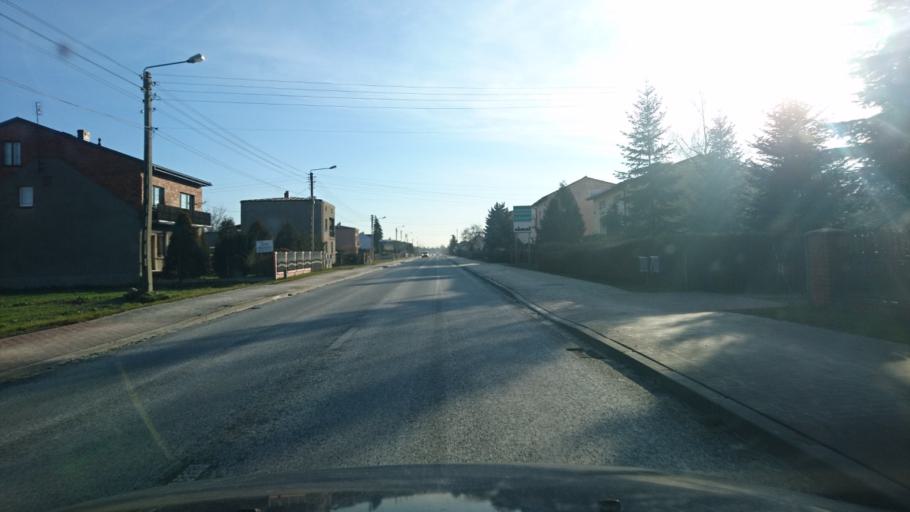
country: PL
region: Silesian Voivodeship
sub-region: Powiat klobucki
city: Starokrzepice
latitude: 51.0126
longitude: 18.6556
